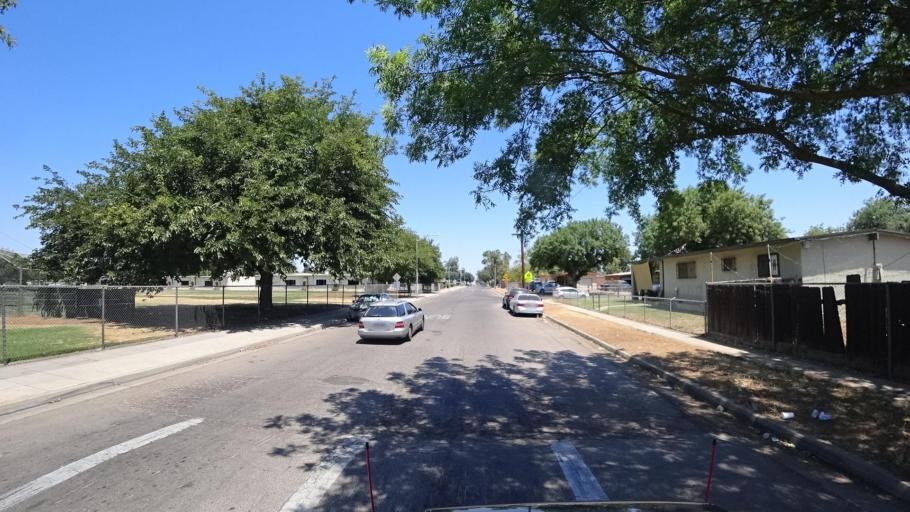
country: US
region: California
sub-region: Fresno County
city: West Park
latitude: 36.7249
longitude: -119.8176
